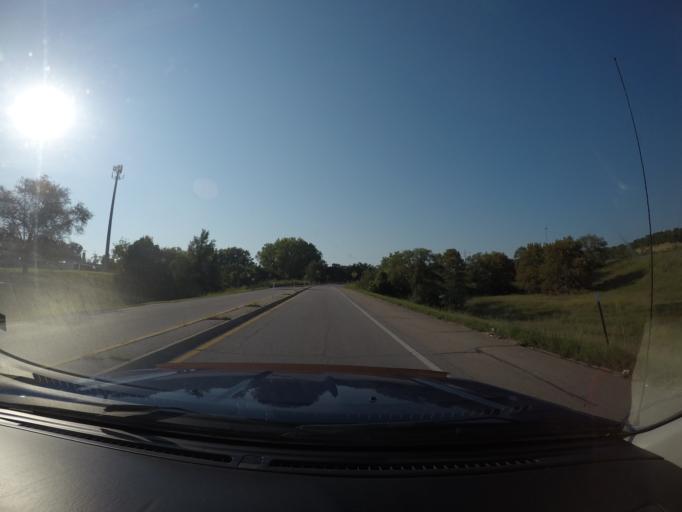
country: US
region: Kansas
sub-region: Wyandotte County
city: Bonner Springs
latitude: 39.0614
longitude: -94.8750
